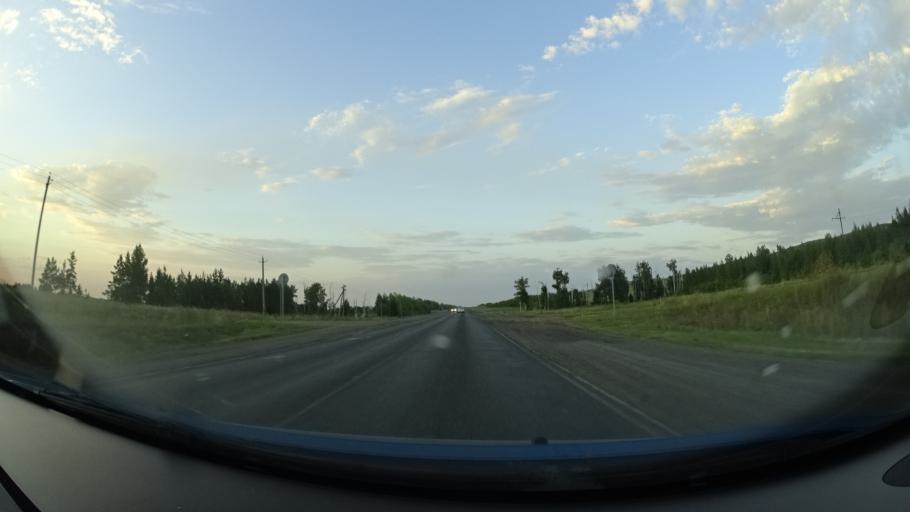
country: RU
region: Orenburg
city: Severnoye
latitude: 54.1882
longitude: 52.6702
